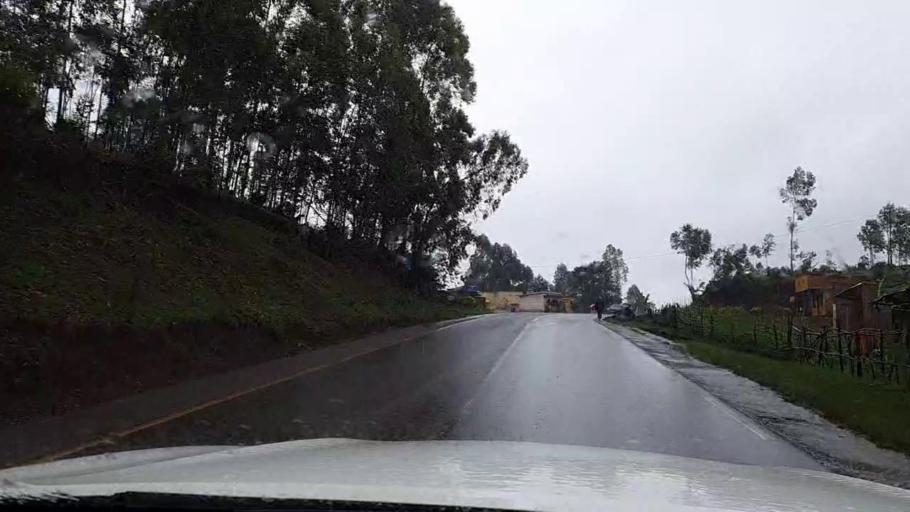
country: RW
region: Western Province
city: Cyangugu
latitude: -2.4628
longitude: 29.0003
